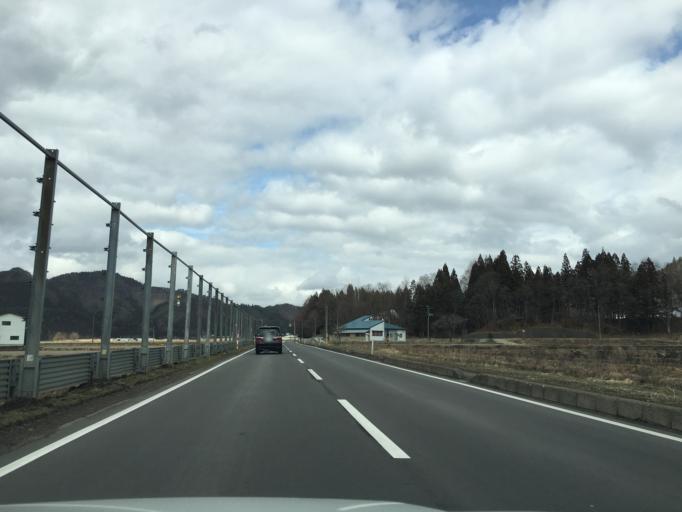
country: JP
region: Akita
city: Hanawa
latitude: 40.2343
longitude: 140.7348
